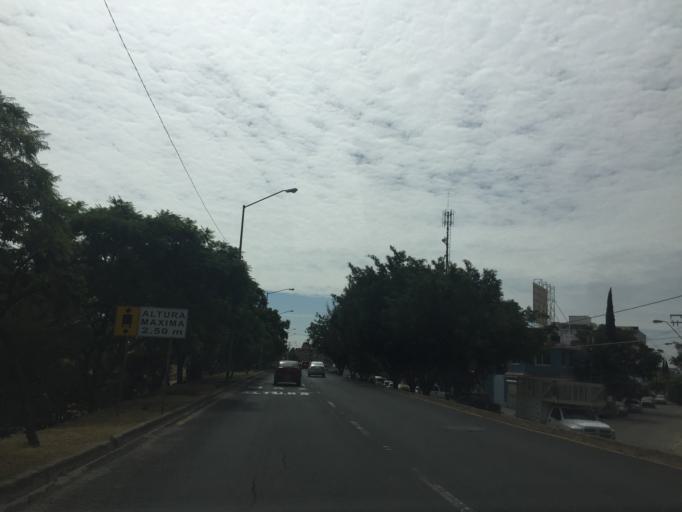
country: MX
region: Guanajuato
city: Leon
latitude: 21.1063
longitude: -101.6621
